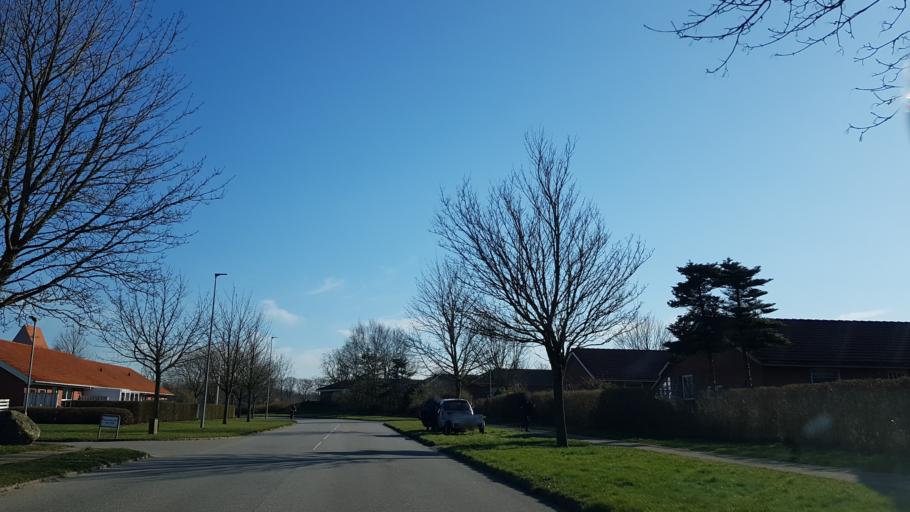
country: DK
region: South Denmark
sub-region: Kolding Kommune
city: Vamdrup
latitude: 55.4307
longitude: 9.2702
